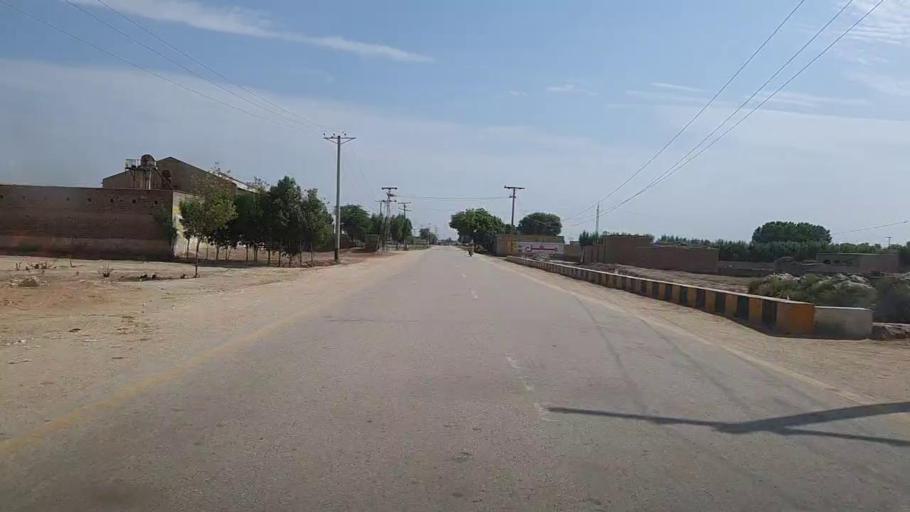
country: PK
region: Sindh
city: Thul
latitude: 28.2358
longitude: 68.7900
